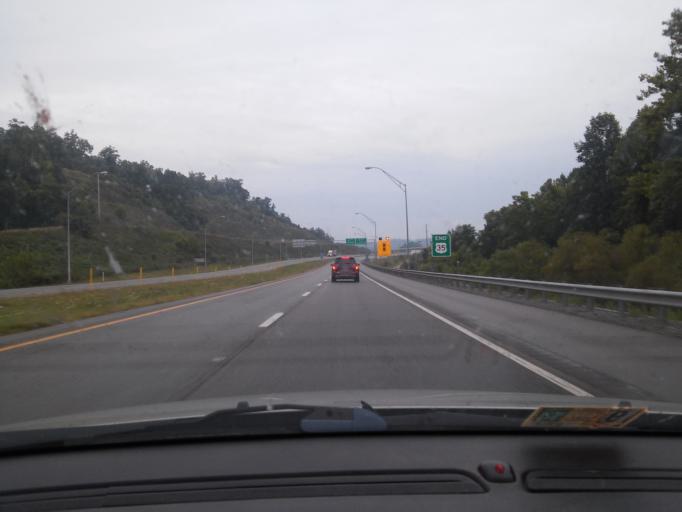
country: US
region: West Virginia
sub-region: Putnam County
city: Teays Valley
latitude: 38.4621
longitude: -81.9066
